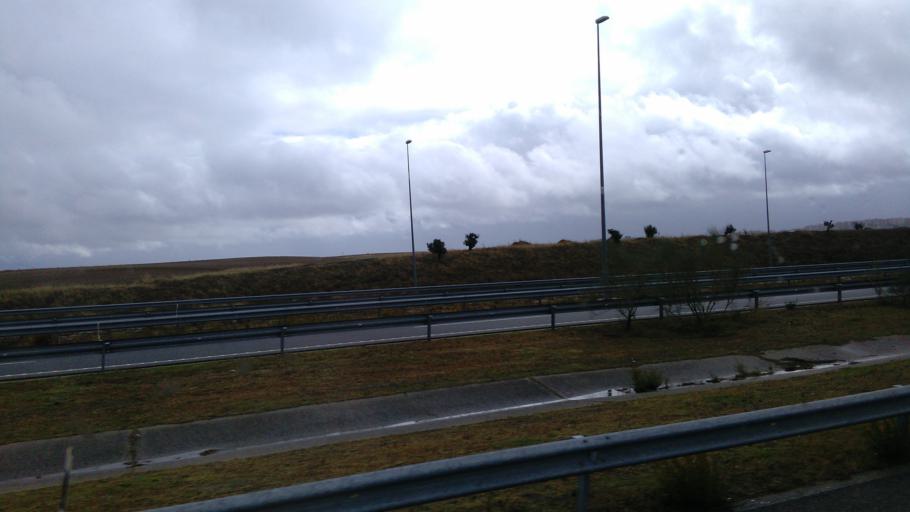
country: ES
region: Madrid
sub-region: Provincia de Madrid
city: Alcorcon
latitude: 40.3247
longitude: -3.8176
